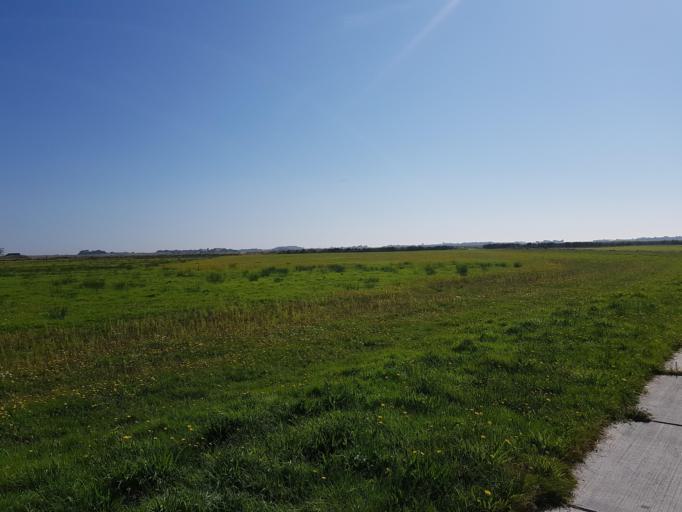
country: NL
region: North Holland
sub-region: Gemeente Texel
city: Den Burg
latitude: 53.0916
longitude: 4.8010
